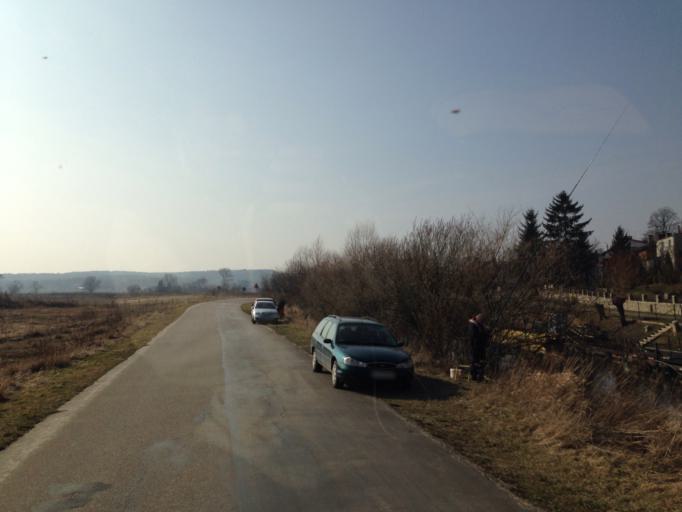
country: PL
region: Pomeranian Voivodeship
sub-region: Powiat tczewski
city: Gniew
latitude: 53.8330
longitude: 18.8304
